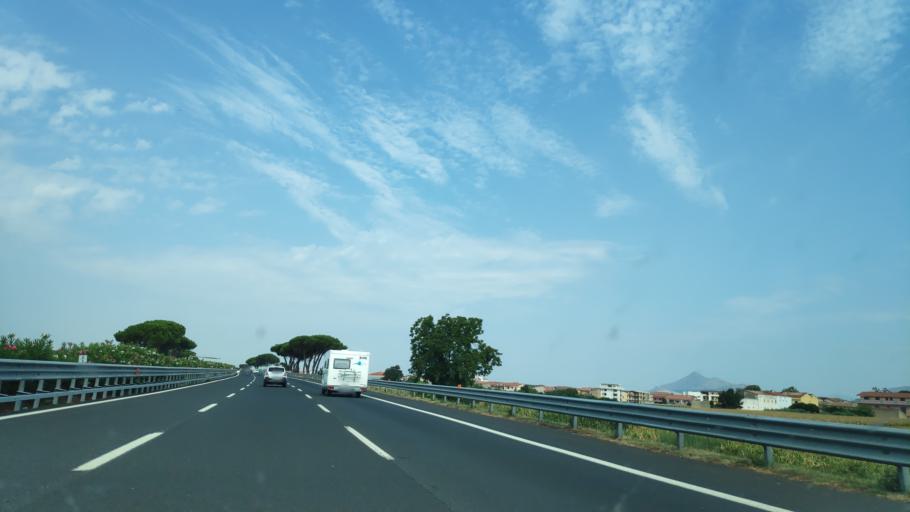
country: IT
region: Campania
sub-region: Provincia di Caserta
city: San Marco Evangelista
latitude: 41.0303
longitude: 14.3475
